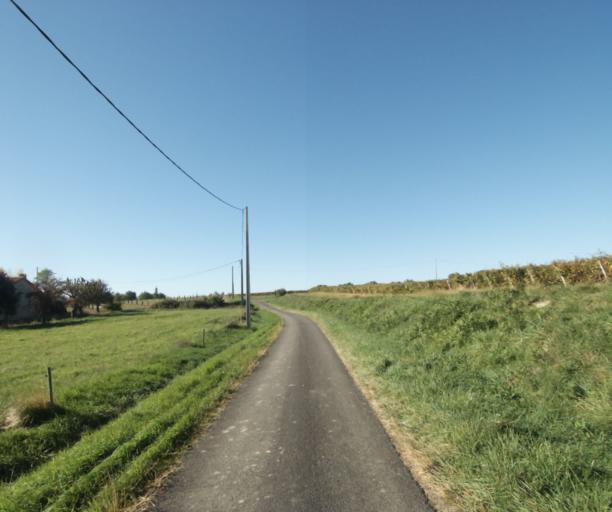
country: FR
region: Midi-Pyrenees
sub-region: Departement du Gers
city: Gondrin
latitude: 43.8201
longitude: 0.2353
